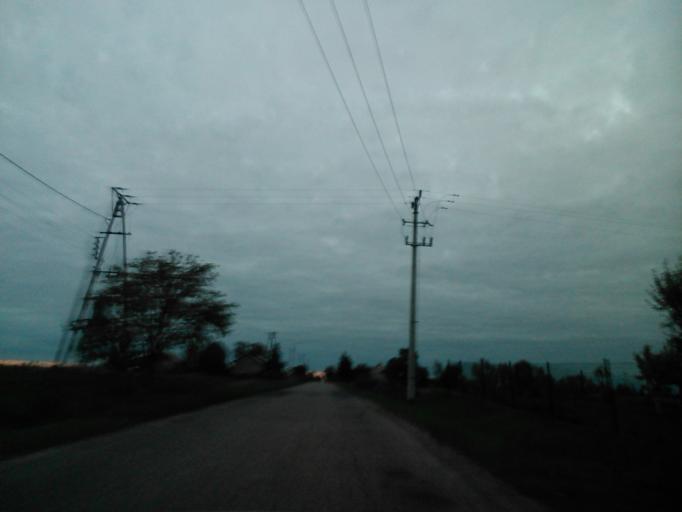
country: PL
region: Kujawsko-Pomorskie
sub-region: Powiat golubsko-dobrzynski
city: Kowalewo Pomorskie
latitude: 53.1109
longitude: 18.8930
